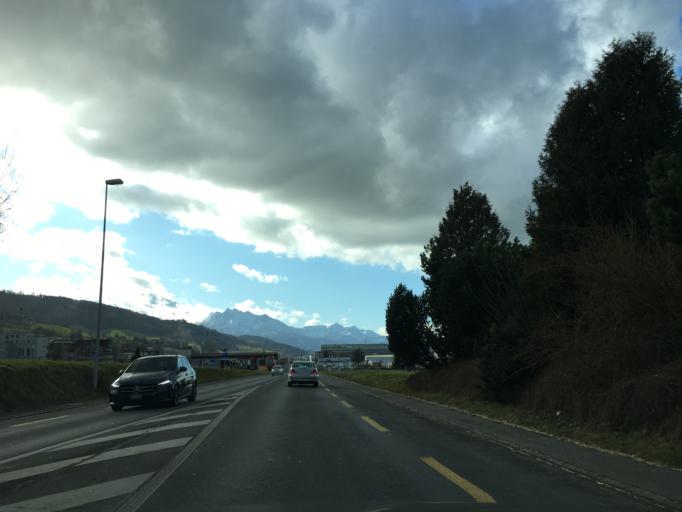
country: CH
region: Lucerne
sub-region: Lucerne-Land District
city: Root
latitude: 47.1086
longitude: 8.3828
